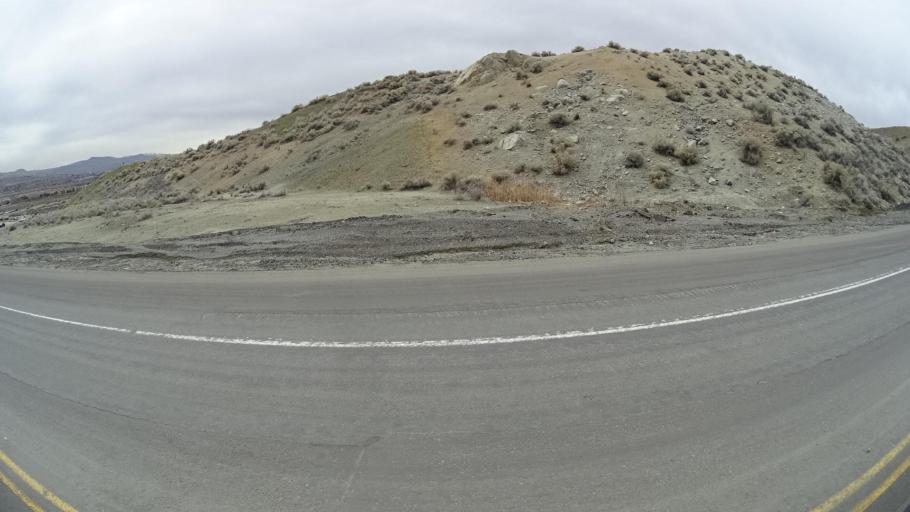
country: US
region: Nevada
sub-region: Washoe County
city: Sun Valley
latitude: 39.6113
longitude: -119.7350
